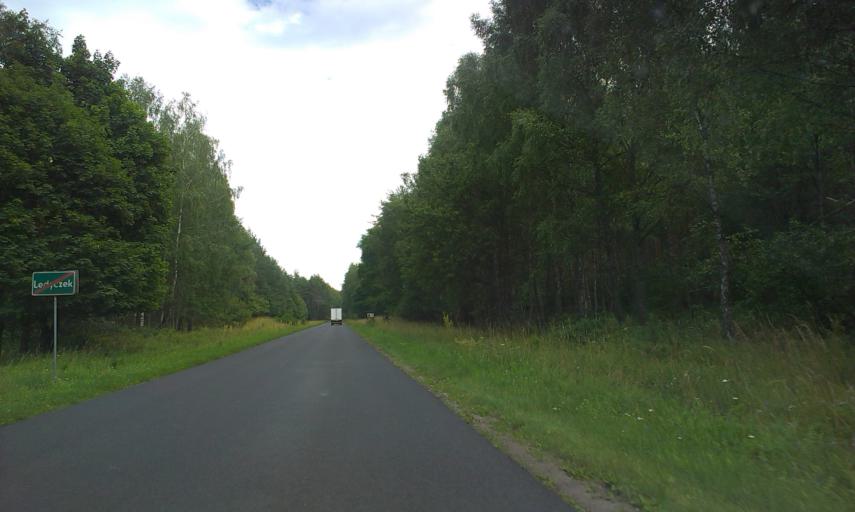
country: PL
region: Greater Poland Voivodeship
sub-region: Powiat zlotowski
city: Okonek
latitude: 53.5303
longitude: 16.9555
